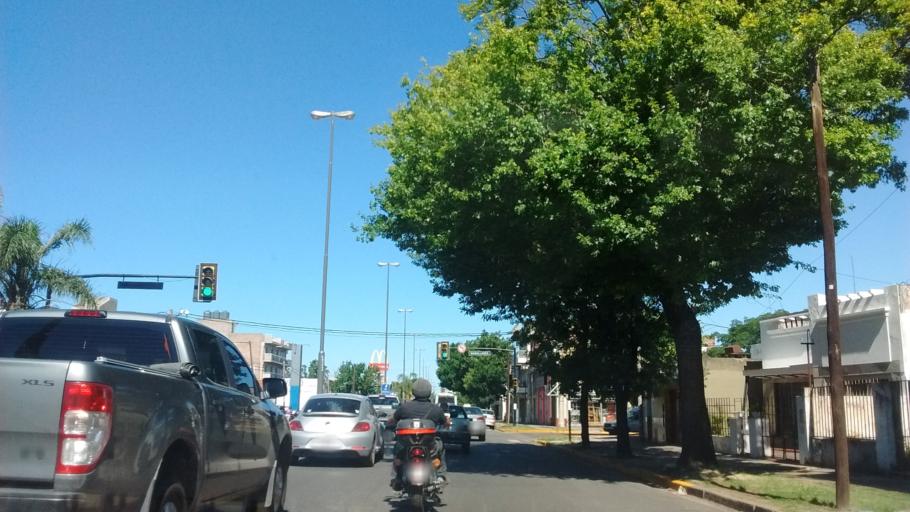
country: AR
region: Santa Fe
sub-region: Departamento de Rosario
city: Rosario
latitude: -32.9344
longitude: -60.7053
